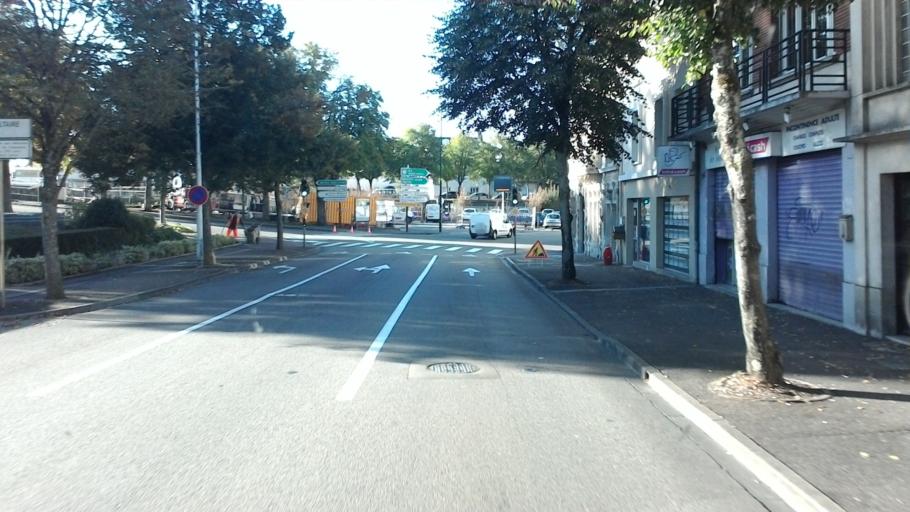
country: FR
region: Champagne-Ardenne
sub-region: Departement de la Haute-Marne
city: Chaumont
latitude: 48.1106
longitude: 5.1425
